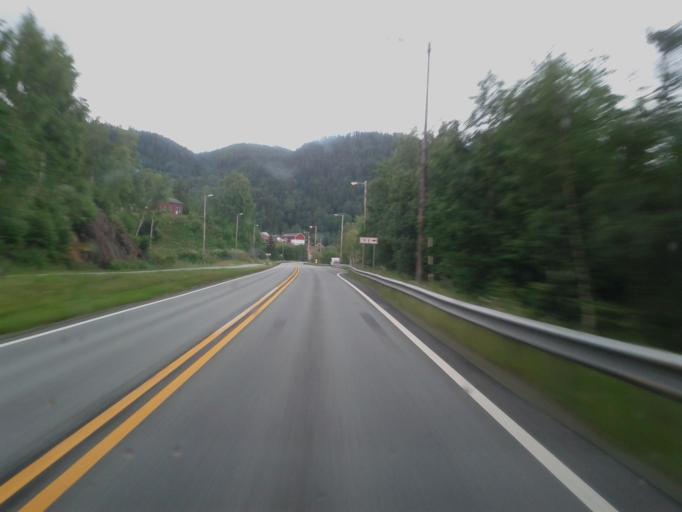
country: NO
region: Sor-Trondelag
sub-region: Midtre Gauldal
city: Storen
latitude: 63.0935
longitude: 10.2426
